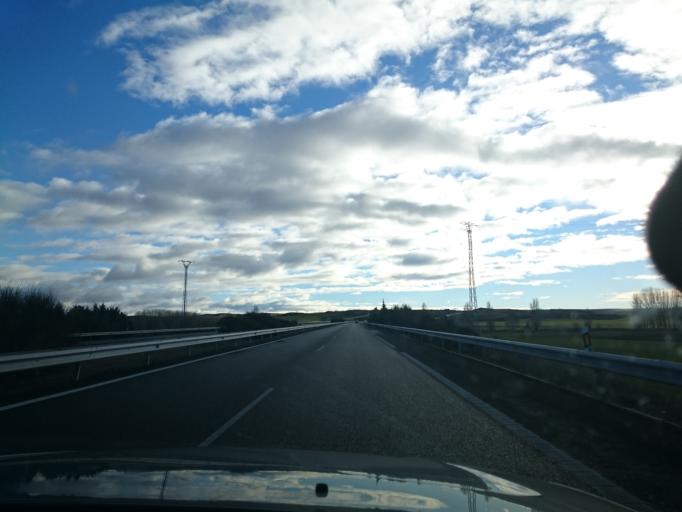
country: ES
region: Castille and Leon
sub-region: Provincia de Leon
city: Sahagun
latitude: 42.3750
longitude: -4.9995
